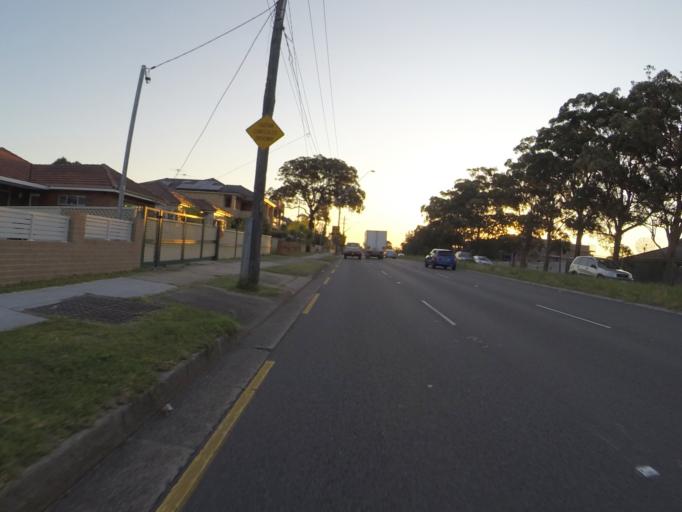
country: AU
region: New South Wales
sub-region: Hurstville
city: Peakhurst
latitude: -33.9605
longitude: 151.0604
